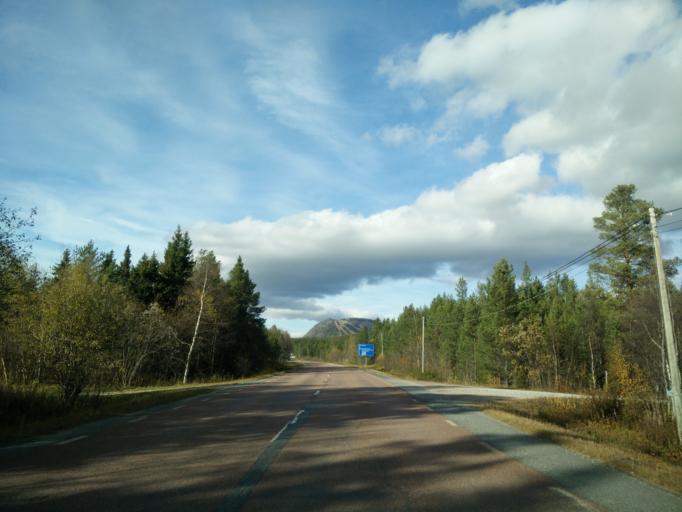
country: NO
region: Hedmark
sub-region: Engerdal
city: Engerdal
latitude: 62.5205
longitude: 12.5942
